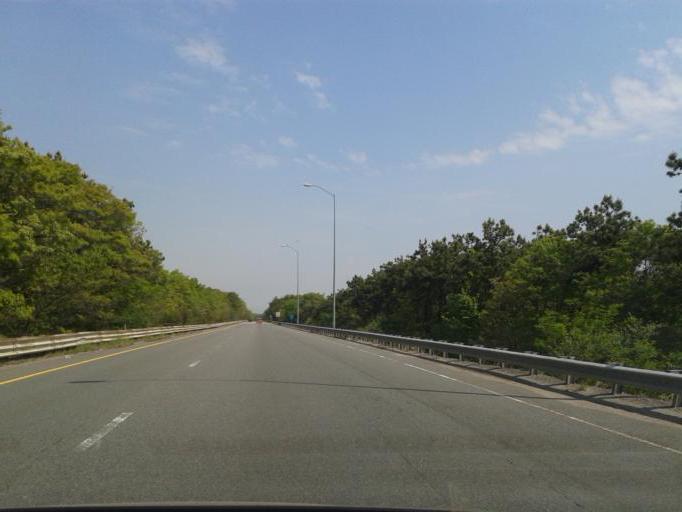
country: US
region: Massachusetts
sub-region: Barnstable County
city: Sagamore
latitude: 41.7867
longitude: -70.5438
